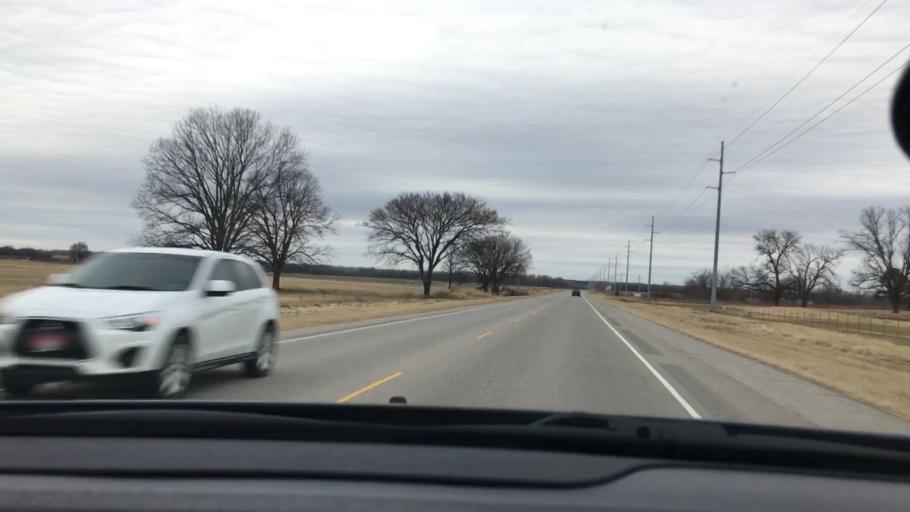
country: US
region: Oklahoma
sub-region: Marshall County
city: Oakland
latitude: 34.1981
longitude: -96.8022
